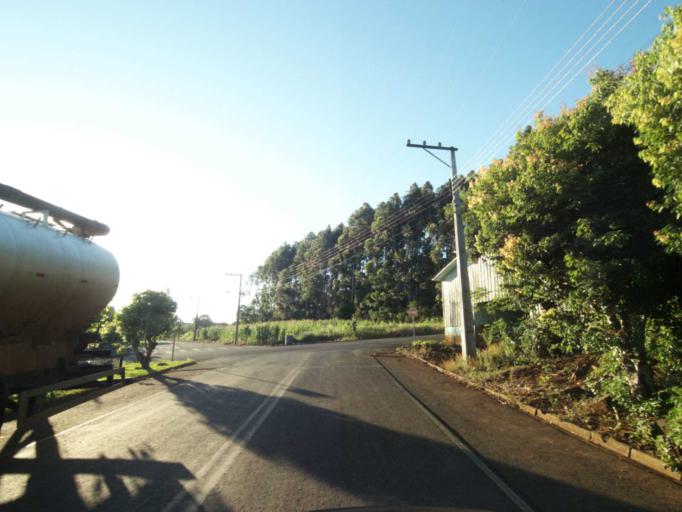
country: BR
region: Parana
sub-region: Coronel Vivida
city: Coronel Vivida
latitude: -25.9751
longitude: -52.8173
